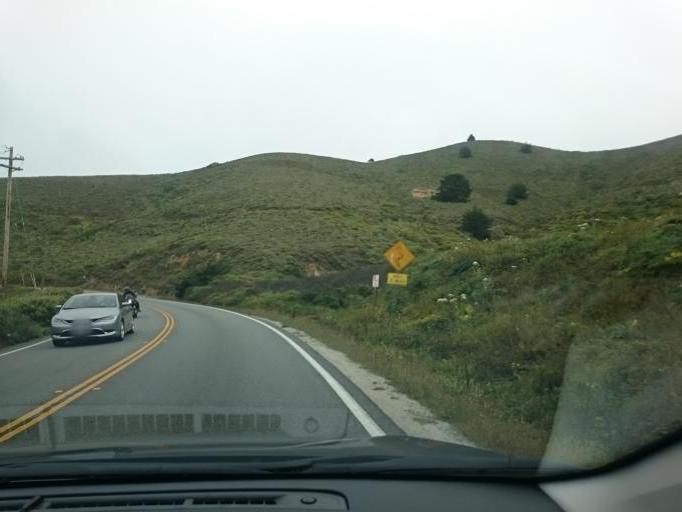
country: US
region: California
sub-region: San Mateo County
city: Montara
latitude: 37.5597
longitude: -122.5134
